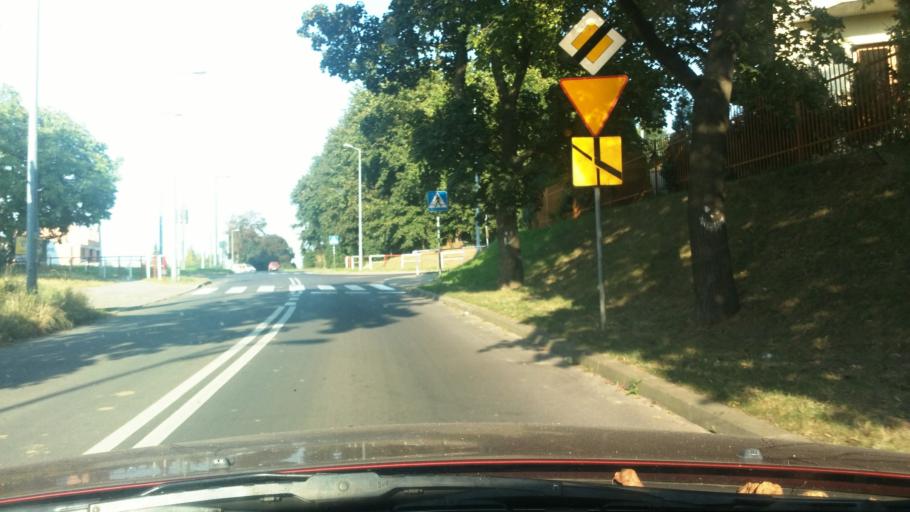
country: DE
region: Saxony
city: Goerlitz
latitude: 51.1598
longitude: 14.9981
